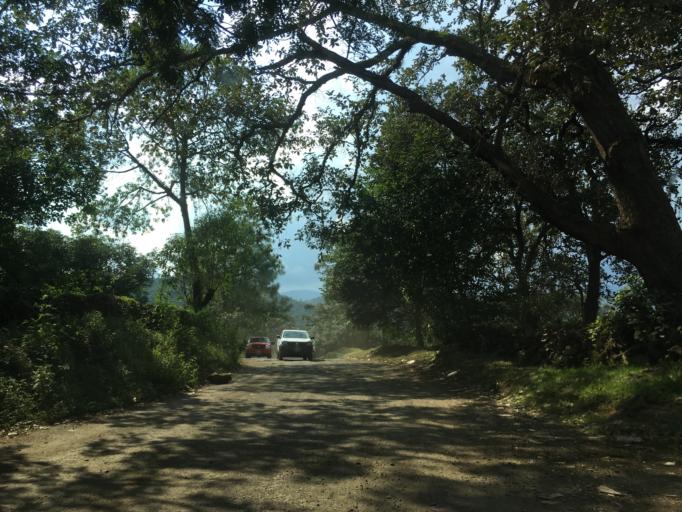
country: MX
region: Michoacan
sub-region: Ziracuaretiro
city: Patuan
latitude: 19.4393
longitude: -101.8791
